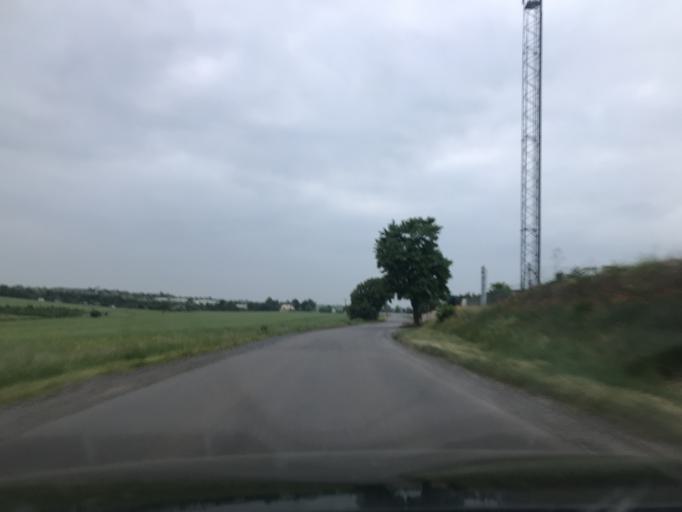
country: DE
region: Saxony-Anhalt
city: Angersdorf
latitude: 51.4565
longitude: 11.8921
